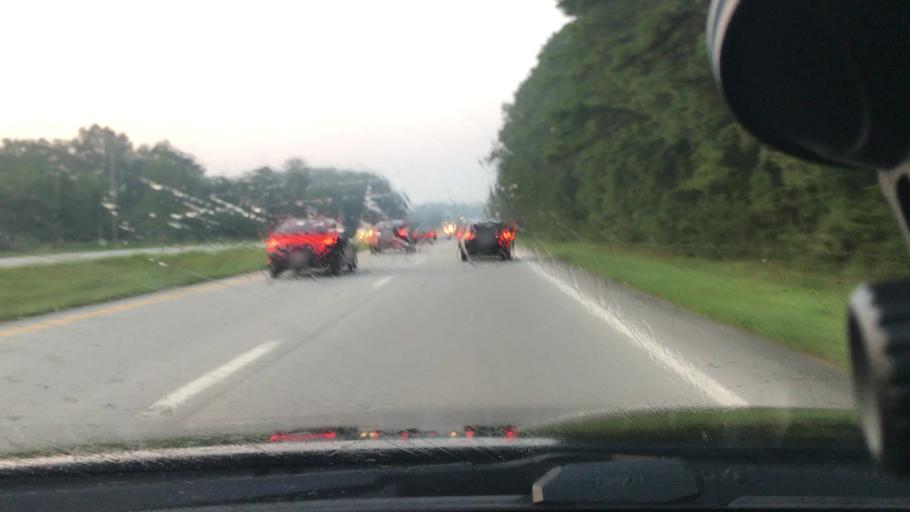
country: US
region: North Carolina
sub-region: Craven County
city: Neuse Forest
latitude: 34.9794
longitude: -76.9770
